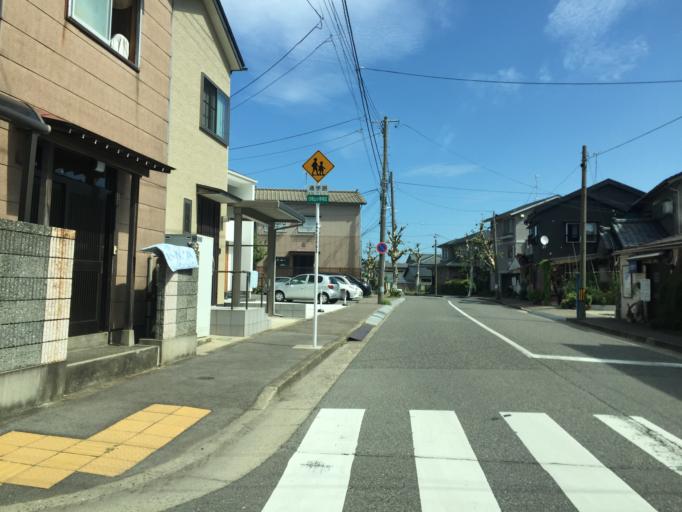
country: JP
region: Niigata
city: Niigata-shi
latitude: 37.9360
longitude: 139.0521
